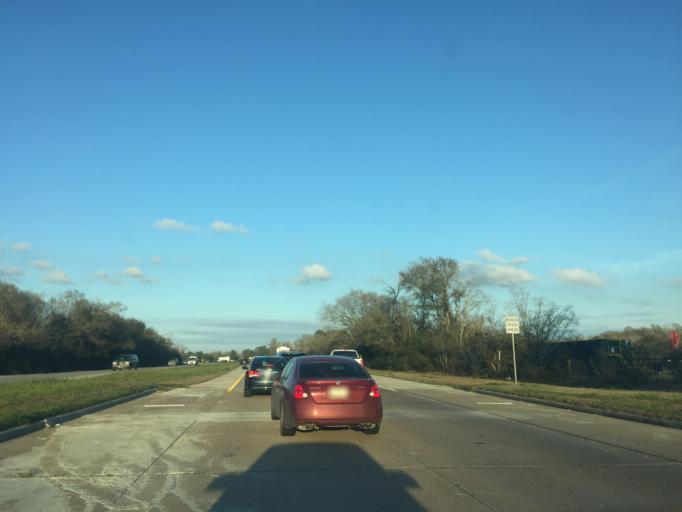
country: US
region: Texas
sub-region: Harris County
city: Baytown
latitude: 29.7198
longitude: -94.9659
